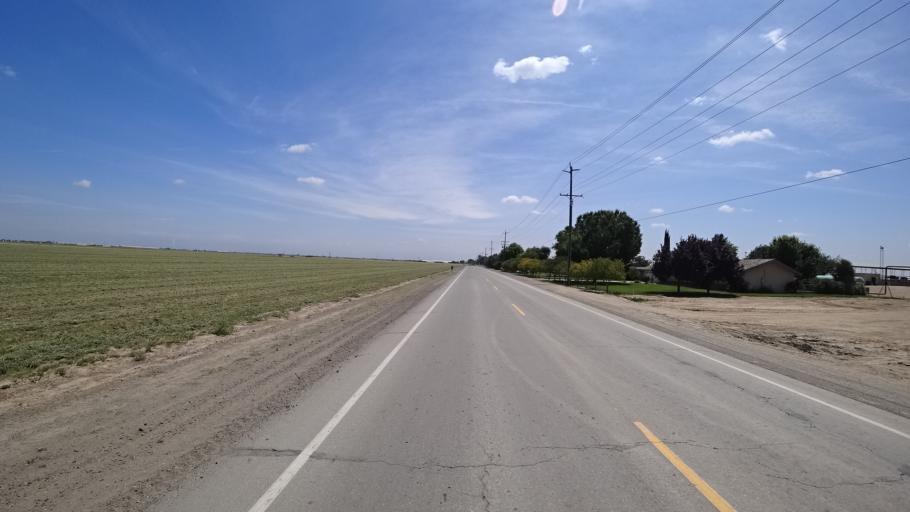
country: US
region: California
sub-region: Kings County
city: Home Garden
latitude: 36.2988
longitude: -119.5416
